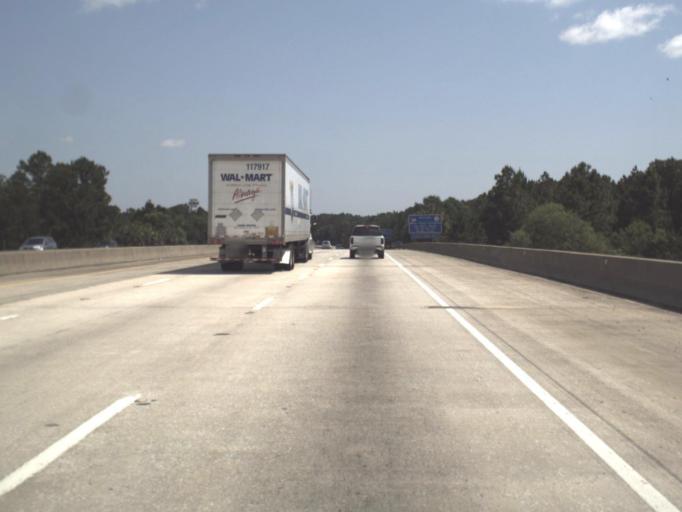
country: US
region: Georgia
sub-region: Camden County
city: Kingsland
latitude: 30.7442
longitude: -81.6541
